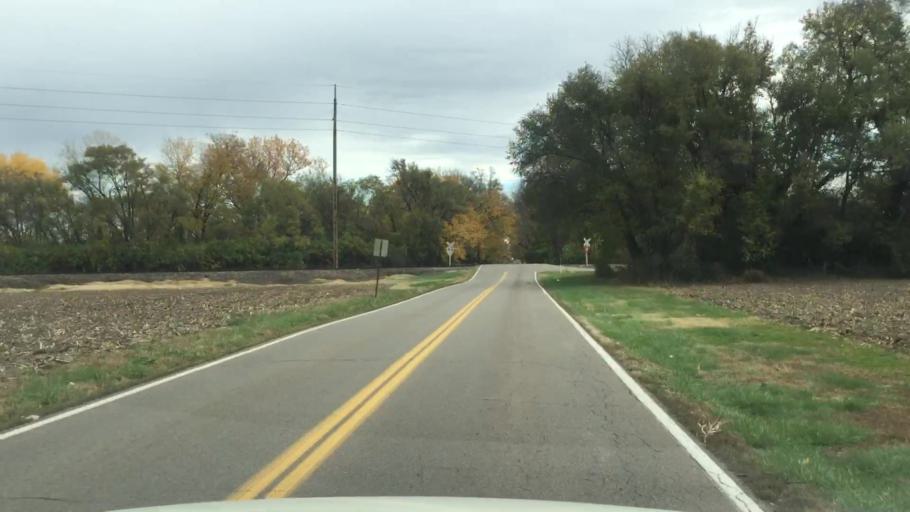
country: US
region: Kansas
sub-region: Shawnee County
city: Topeka
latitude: 39.0876
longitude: -95.6844
